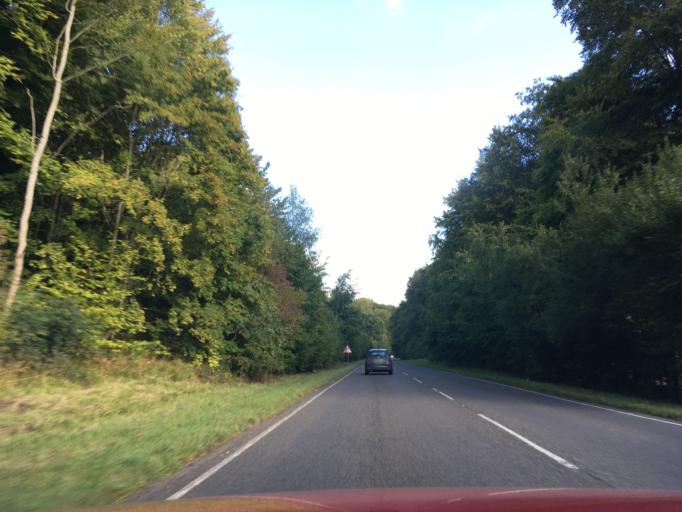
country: GB
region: England
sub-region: Hampshire
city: Alton
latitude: 51.1625
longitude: -1.0153
